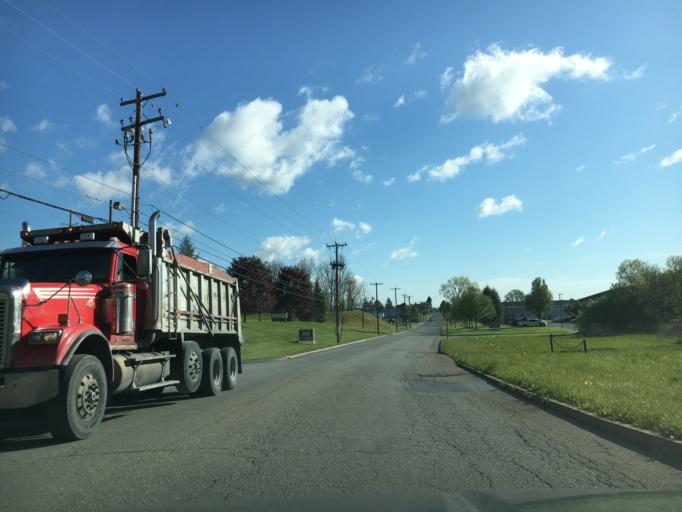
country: US
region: Pennsylvania
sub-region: Lehigh County
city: Stiles
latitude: 40.6729
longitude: -75.5067
